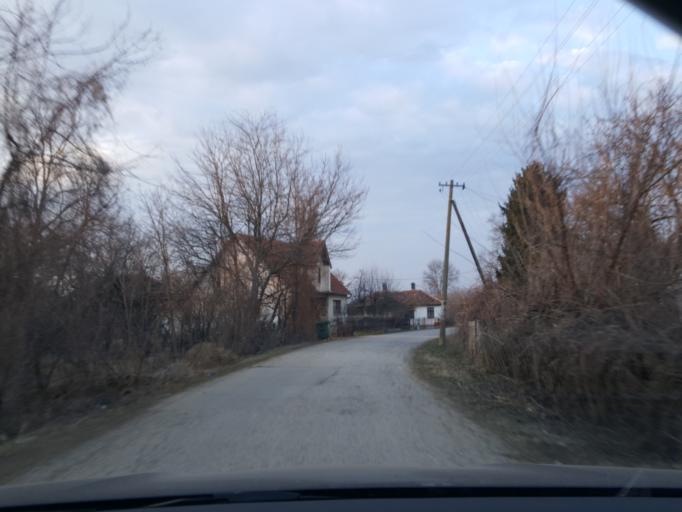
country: RS
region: Central Serbia
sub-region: Nisavski Okrug
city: Aleksinac
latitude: 43.5775
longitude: 21.6463
